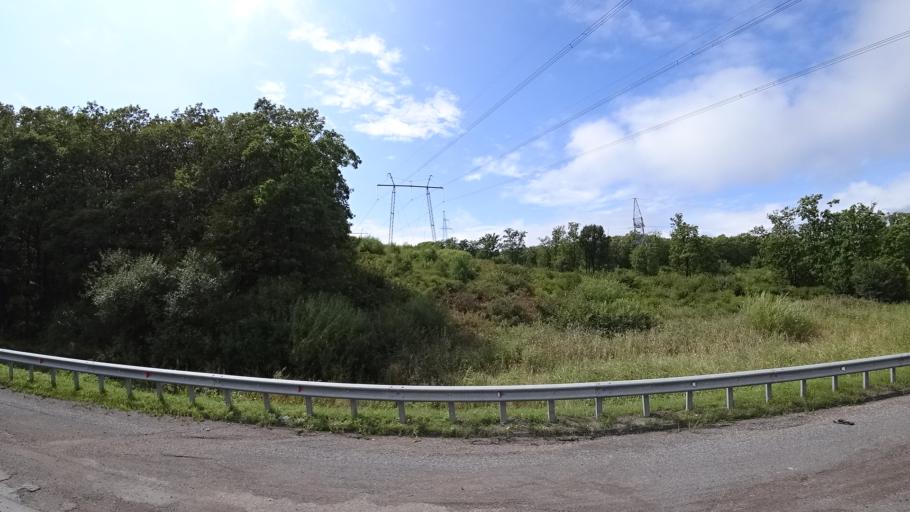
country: RU
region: Primorskiy
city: Lyalichi
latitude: 44.1330
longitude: 132.4273
